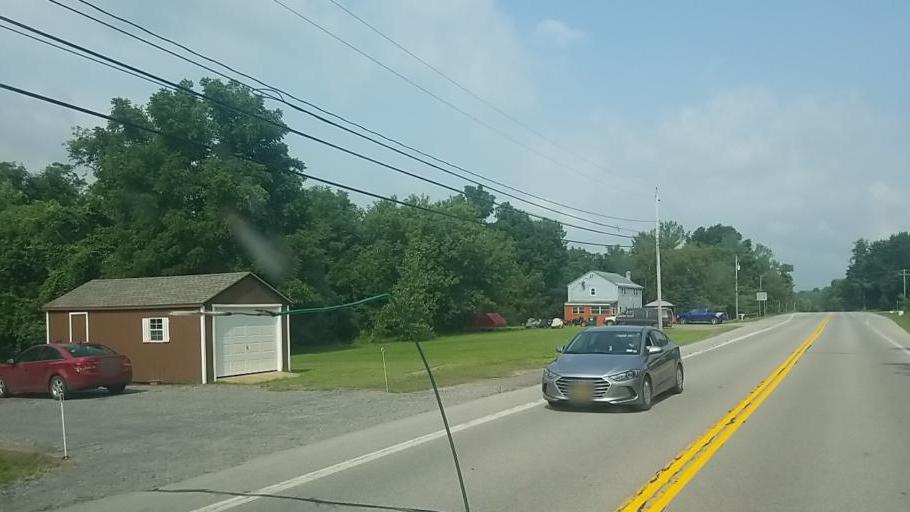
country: US
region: New York
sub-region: Montgomery County
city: Saint Johnsville
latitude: 42.9798
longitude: -74.6403
